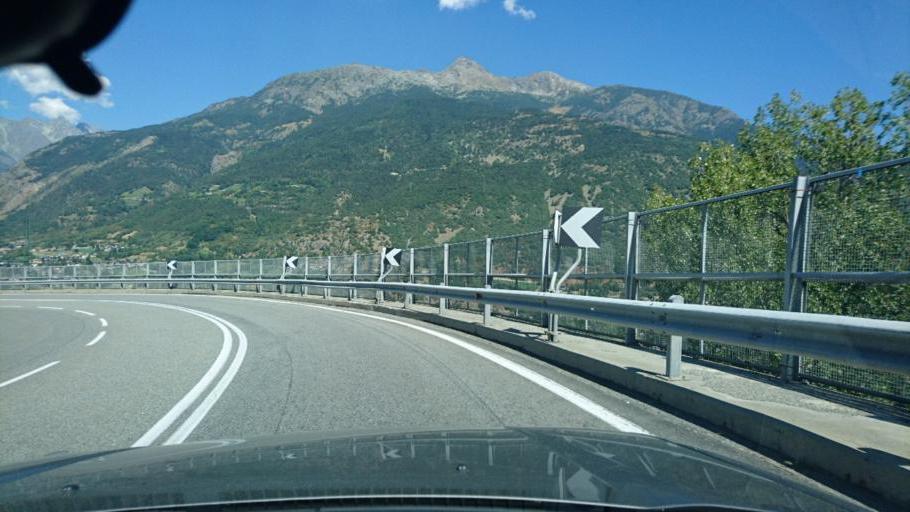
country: IT
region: Aosta Valley
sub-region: Valle d'Aosta
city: Gignod
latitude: 45.7673
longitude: 7.3064
